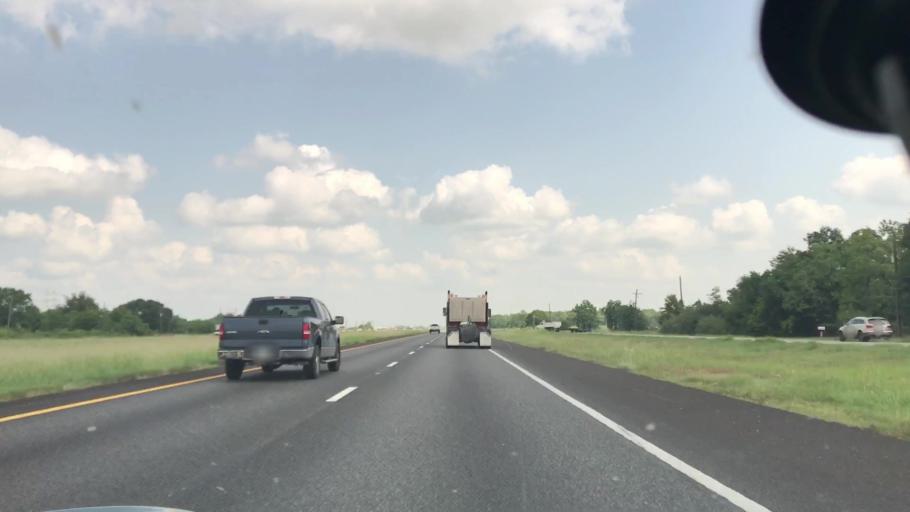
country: US
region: Texas
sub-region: Brazoria County
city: Rosharon
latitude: 29.3978
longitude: -95.4267
